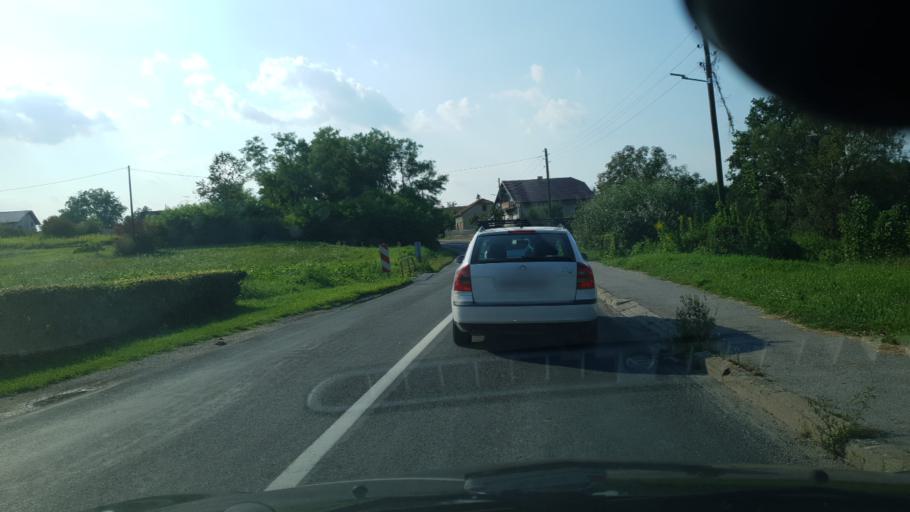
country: HR
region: Krapinsko-Zagorska
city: Oroslavje
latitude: 45.9853
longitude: 15.9201
